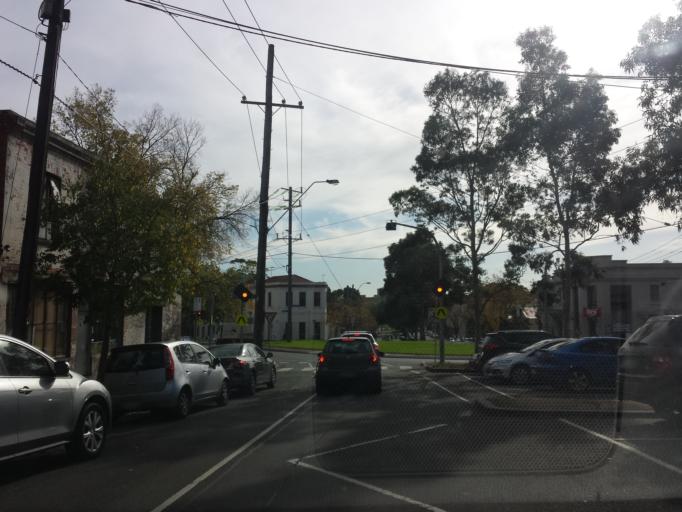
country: AU
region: Victoria
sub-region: Melbourne
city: North Melbourne
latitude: -37.8017
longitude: 144.9534
